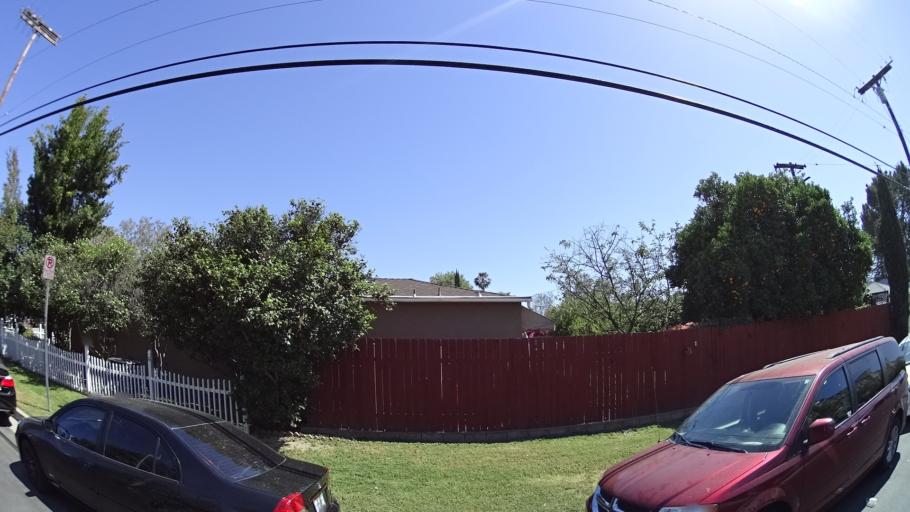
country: US
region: California
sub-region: Los Angeles County
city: North Hollywood
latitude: 34.1704
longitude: -118.3938
